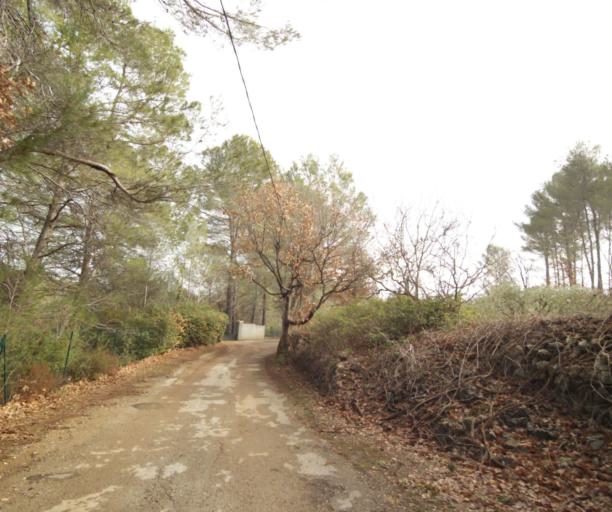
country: FR
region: Provence-Alpes-Cote d'Azur
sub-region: Departement du Var
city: Trans-en-Provence
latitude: 43.5087
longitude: 6.4969
